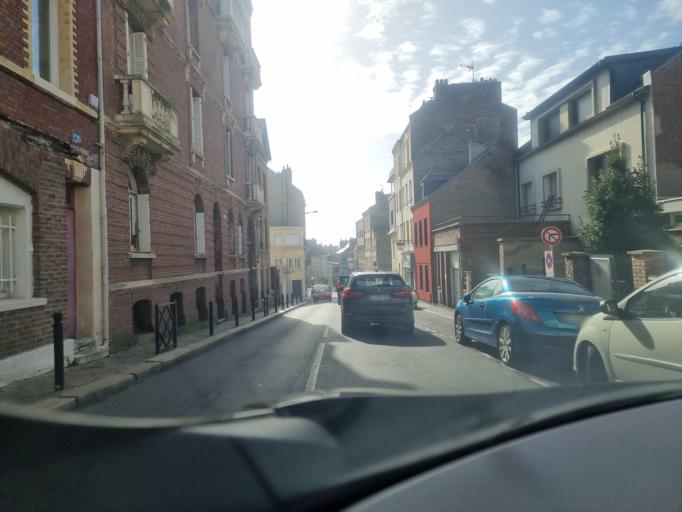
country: FR
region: Haute-Normandie
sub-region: Departement de la Seine-Maritime
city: Le Havre
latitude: 49.4988
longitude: 0.0946
